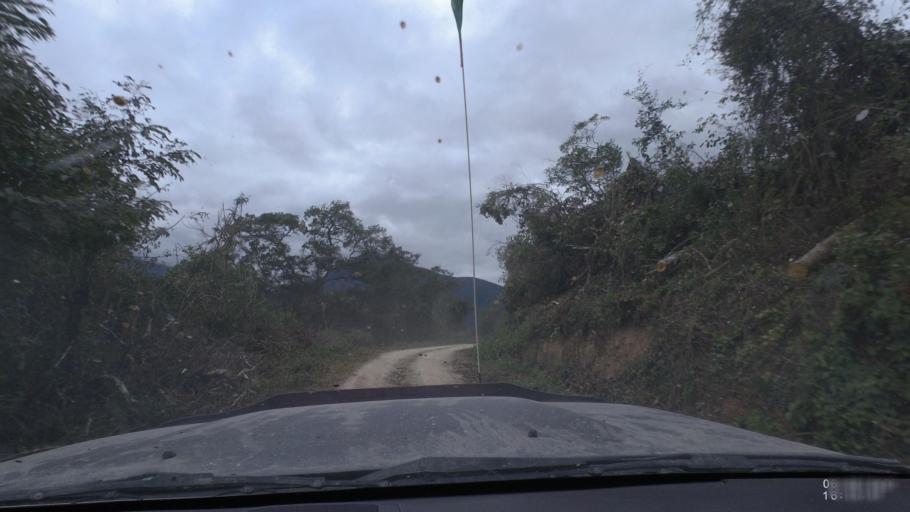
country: BO
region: La Paz
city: Quime
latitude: -16.5285
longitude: -66.7635
